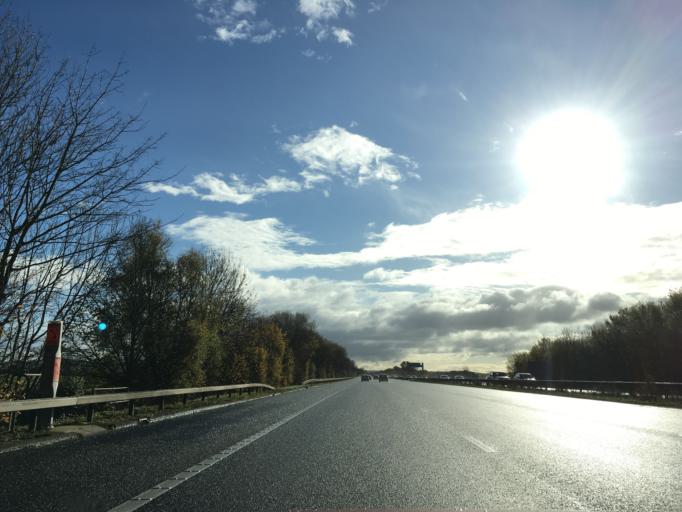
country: GB
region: England
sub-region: Worcestershire
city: Bredon
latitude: 52.0300
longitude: -2.1249
